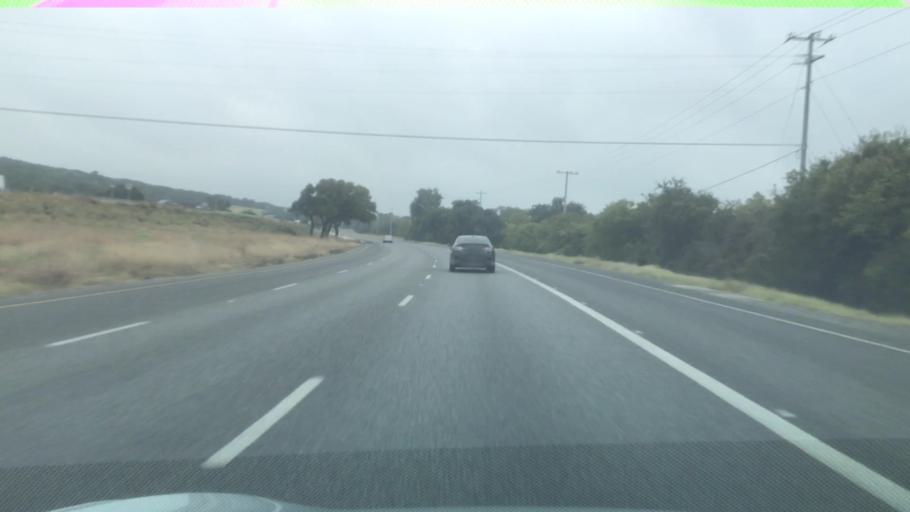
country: US
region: Texas
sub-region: Comal County
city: Canyon Lake
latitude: 29.8962
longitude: -98.4111
